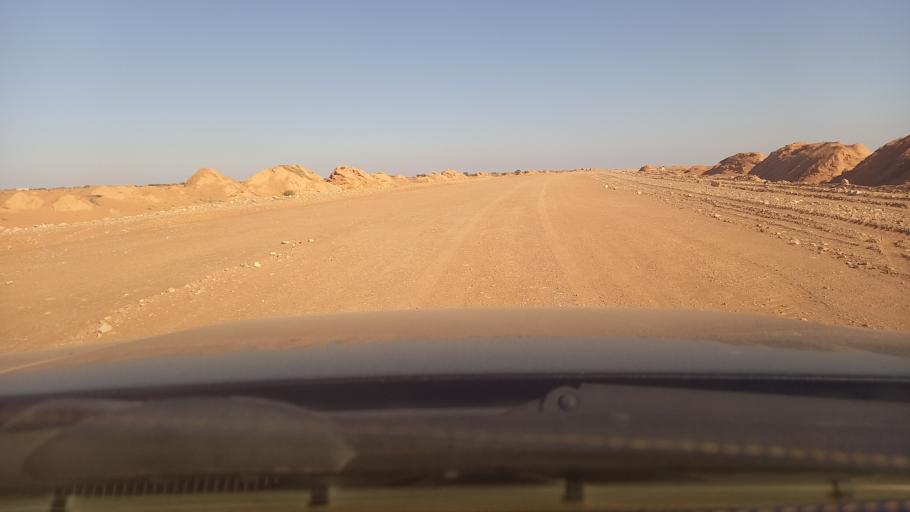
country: TN
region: Madanin
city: Medenine
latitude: 33.1497
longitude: 10.5082
